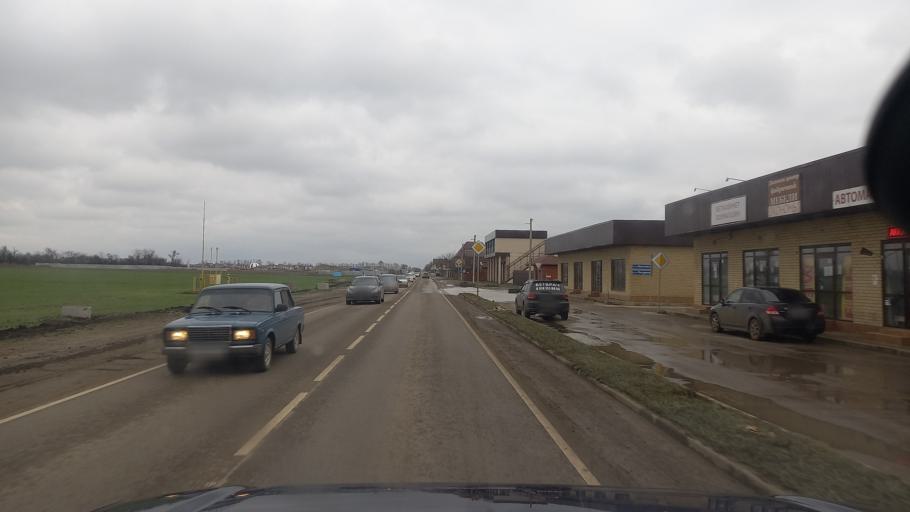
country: RU
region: Krasnodarskiy
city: Pashkovskiy
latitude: 45.0591
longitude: 39.1556
